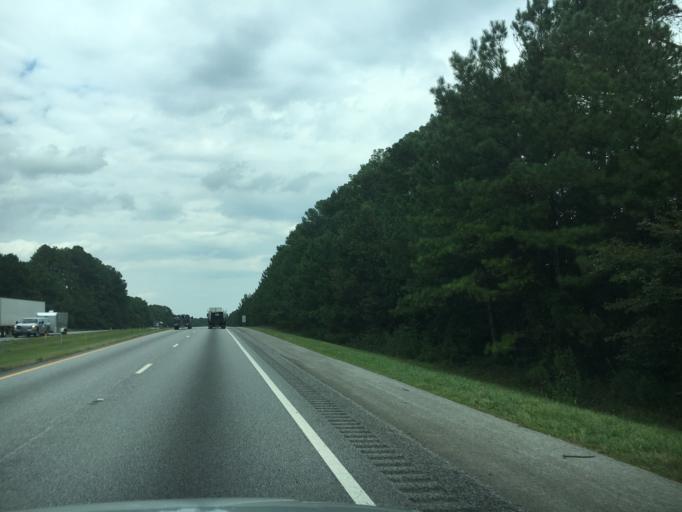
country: US
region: Georgia
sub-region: Hart County
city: Reed Creek
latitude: 34.5082
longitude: -82.9551
